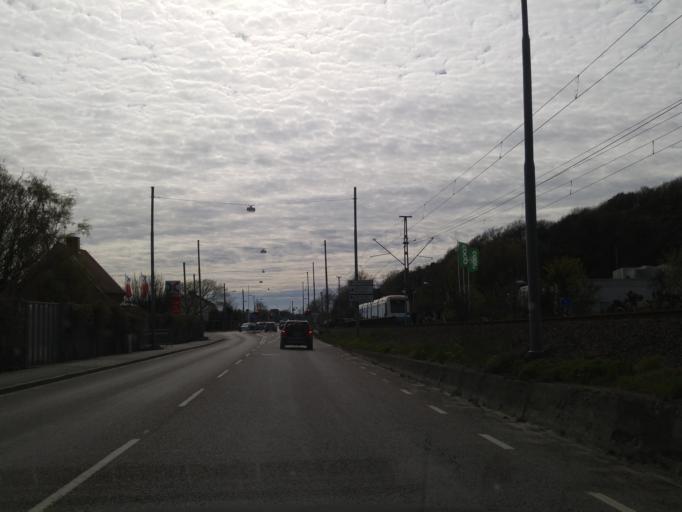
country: SE
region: Vaestra Goetaland
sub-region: Goteborg
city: Majorna
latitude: 57.6698
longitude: 11.8735
